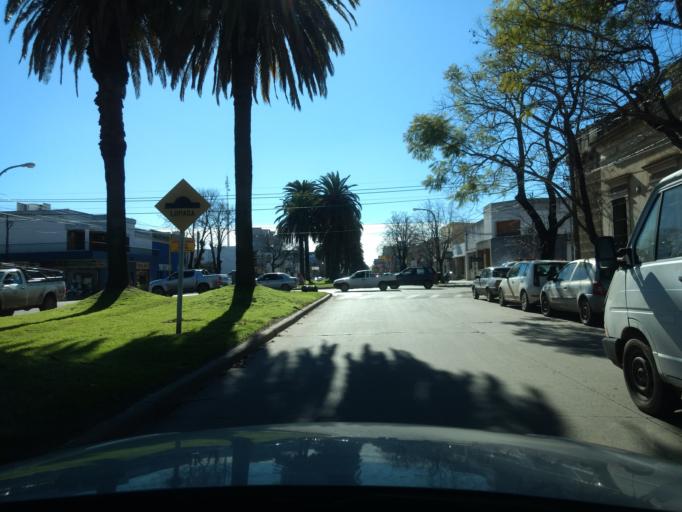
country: AR
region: Buenos Aires
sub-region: Partido de Lujan
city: Lujan
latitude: -34.5694
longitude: -59.1121
